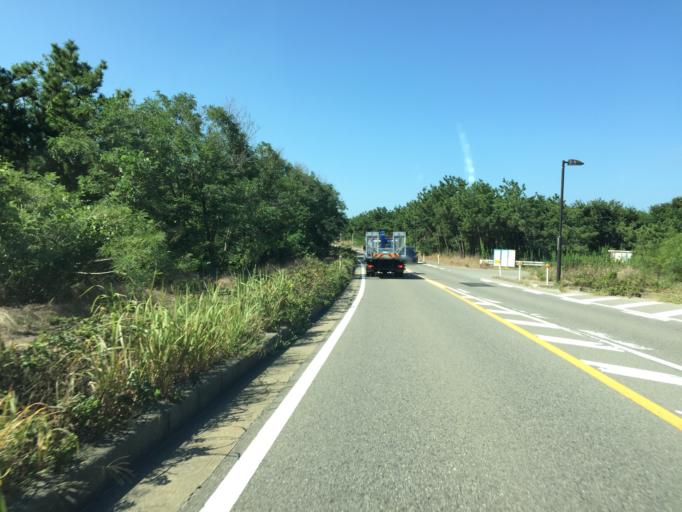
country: JP
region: Niigata
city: Niigata-shi
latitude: 37.9058
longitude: 138.9985
